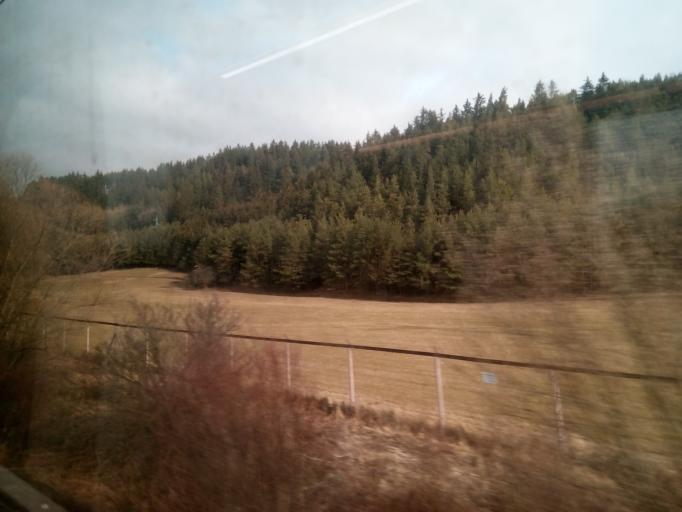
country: SK
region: Zilinsky
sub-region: Okres Zilina
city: Liptovsky Hradok
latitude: 49.0613
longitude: 19.6931
